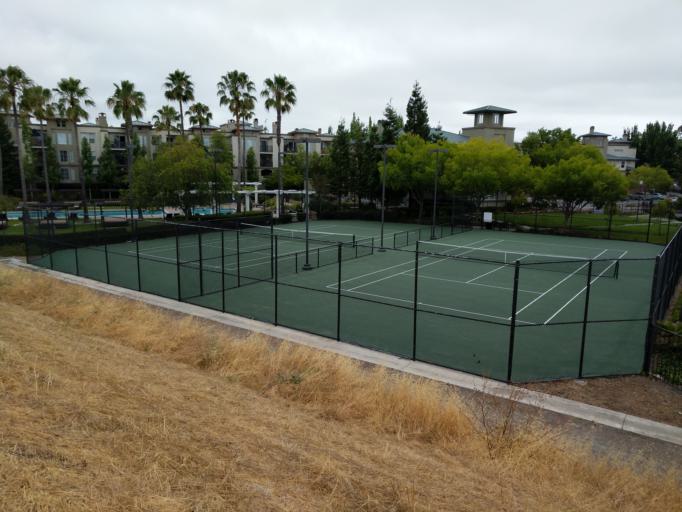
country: US
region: California
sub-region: Santa Clara County
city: Milpitas
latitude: 37.4131
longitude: -121.9628
